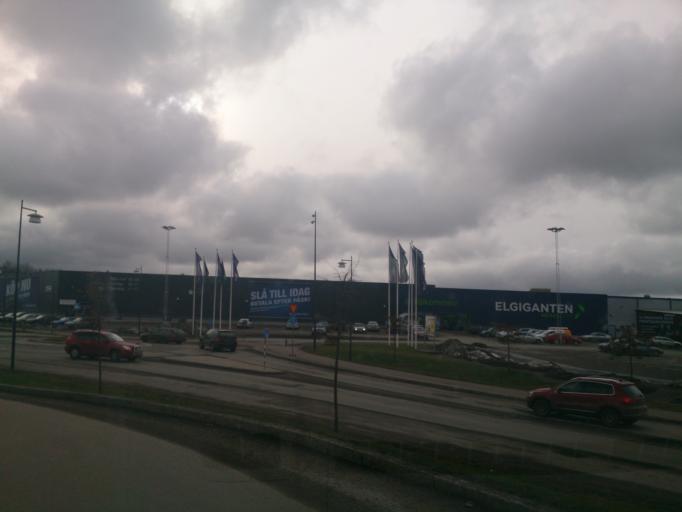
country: SE
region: OEstergoetland
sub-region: Norrkopings Kommun
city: Norrkoping
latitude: 58.6197
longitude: 16.1543
